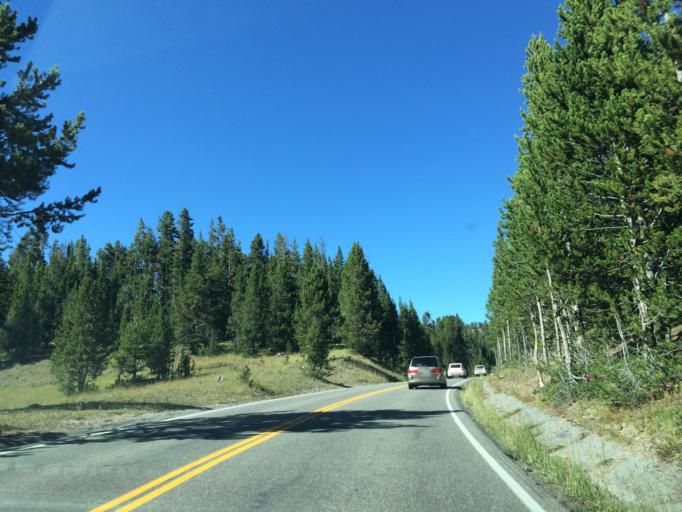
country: US
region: Montana
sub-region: Gallatin County
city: West Yellowstone
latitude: 44.7153
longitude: -110.5049
